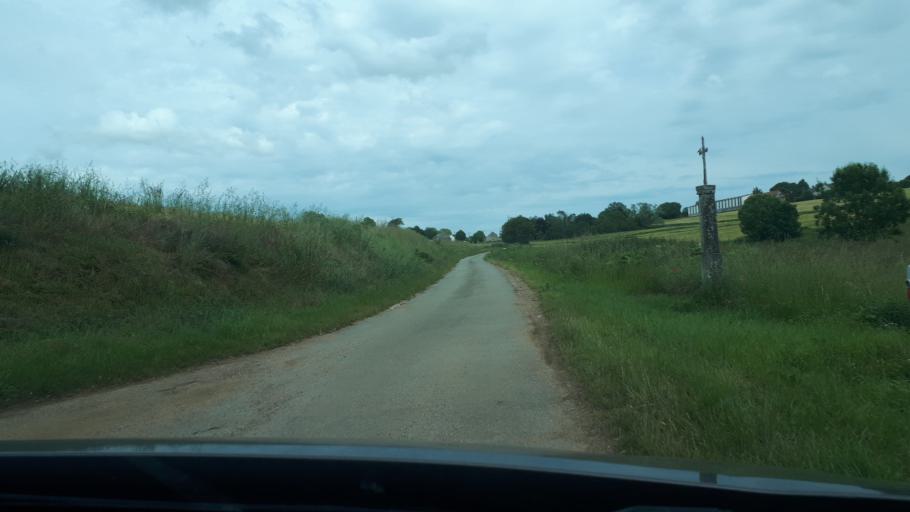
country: FR
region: Centre
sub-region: Departement du Cher
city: Sancerre
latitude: 47.3185
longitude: 2.7330
